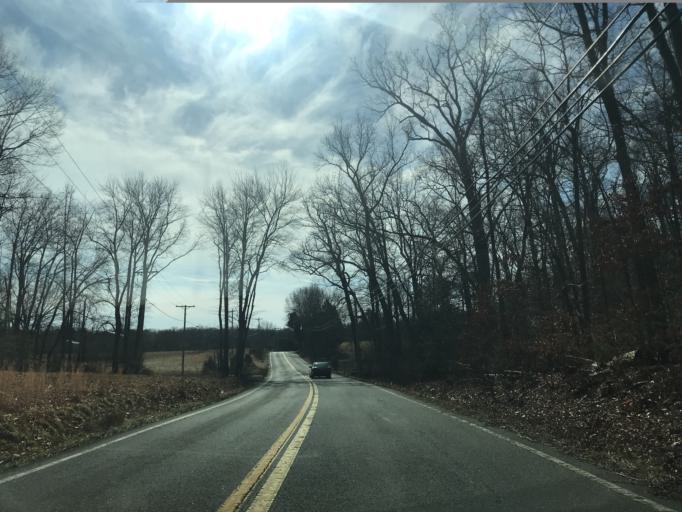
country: US
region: Maryland
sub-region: Charles County
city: Potomac Heights
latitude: 38.5754
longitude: -77.1256
